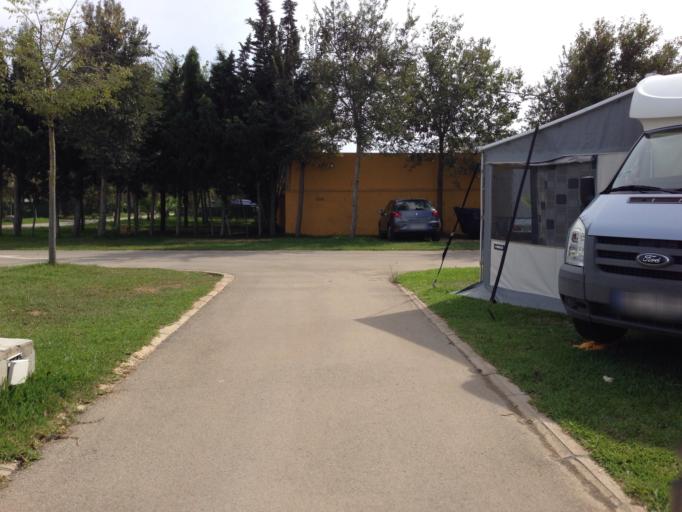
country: ES
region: Andalusia
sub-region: Provincia de Cadiz
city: Conil de la Frontera
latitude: 36.3131
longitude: -6.1138
